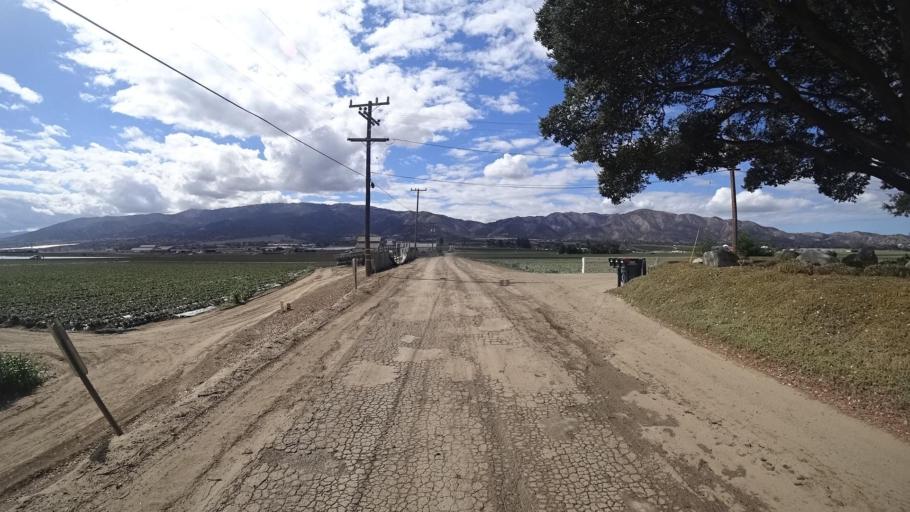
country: US
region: California
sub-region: Monterey County
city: Salinas
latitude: 36.6008
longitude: -121.6059
